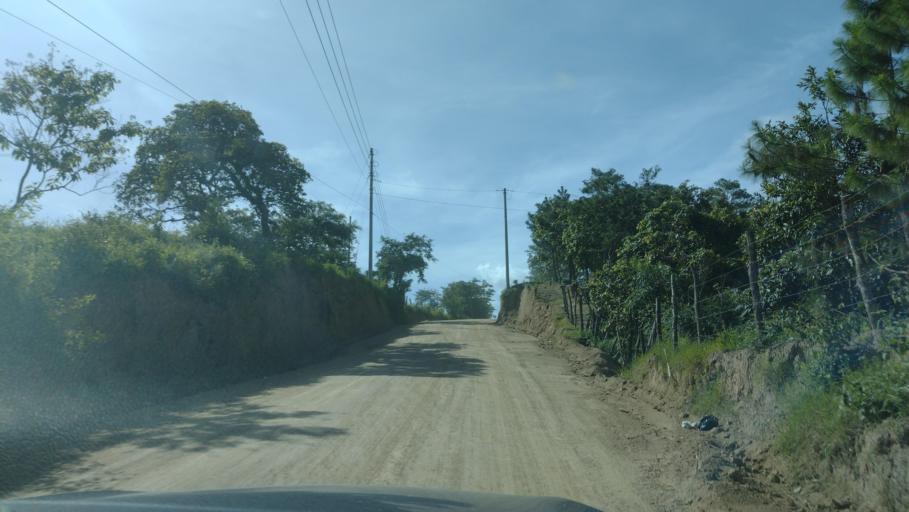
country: GT
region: Guatemala
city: Chinautla
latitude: 14.7578
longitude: -90.5213
